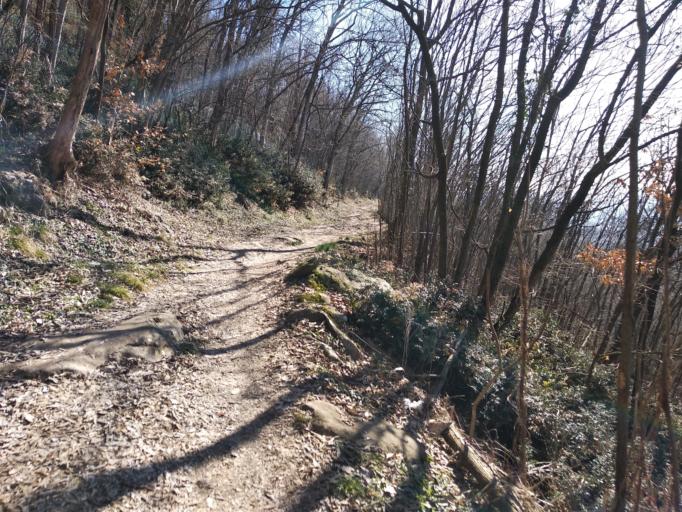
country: IT
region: Veneto
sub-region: Provincia di Vicenza
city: Costabissara
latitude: 45.5822
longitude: 11.4714
